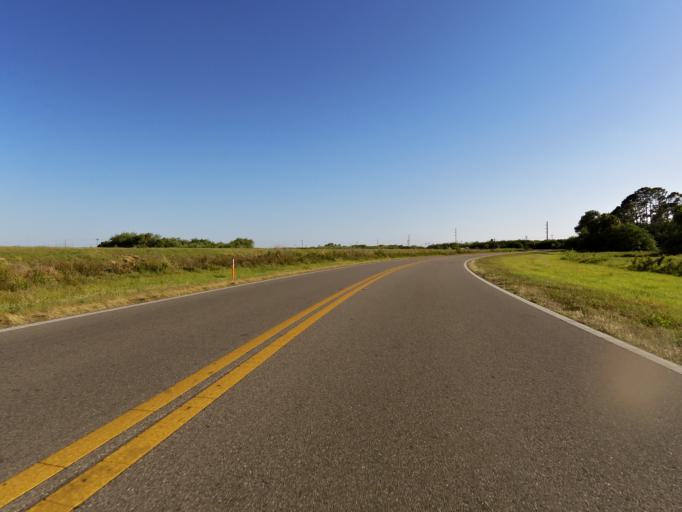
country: US
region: Florida
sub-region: Collier County
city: Immokalee
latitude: 26.3715
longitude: -81.4146
